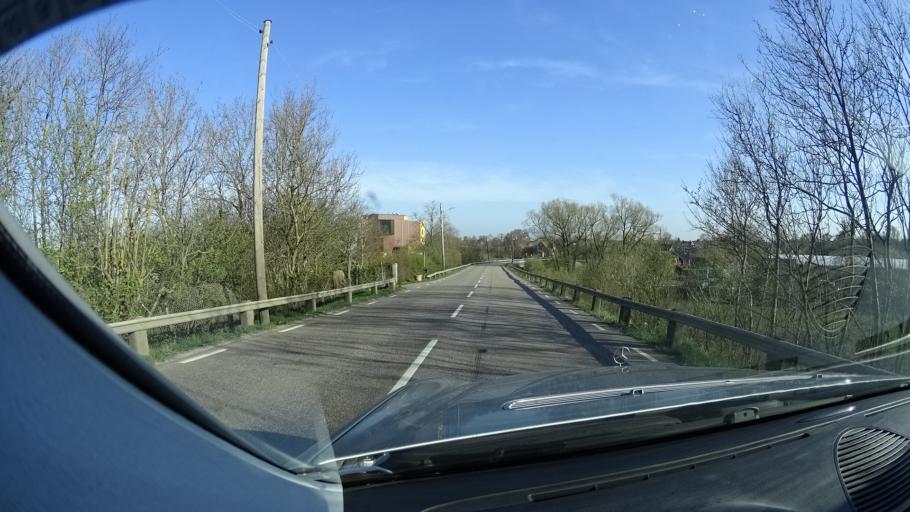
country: SE
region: Skane
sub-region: Landskrona
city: Asmundtorp
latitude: 55.9288
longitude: 12.9543
